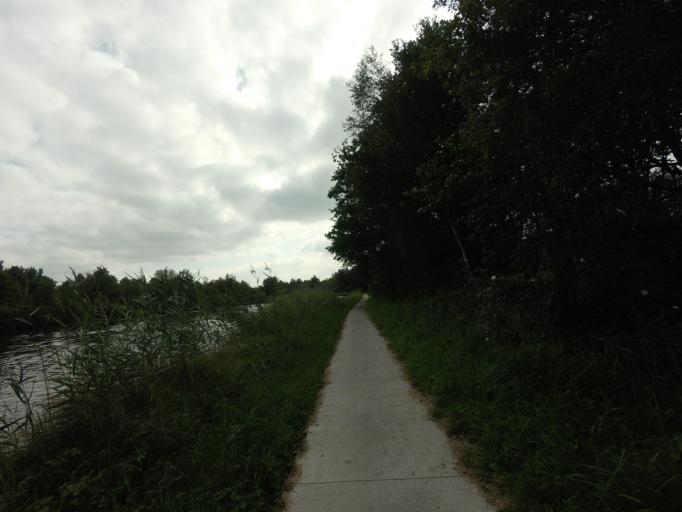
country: NL
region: Overijssel
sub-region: Gemeente Steenwijkerland
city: Oldemarkt
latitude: 52.7850
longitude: 5.9425
